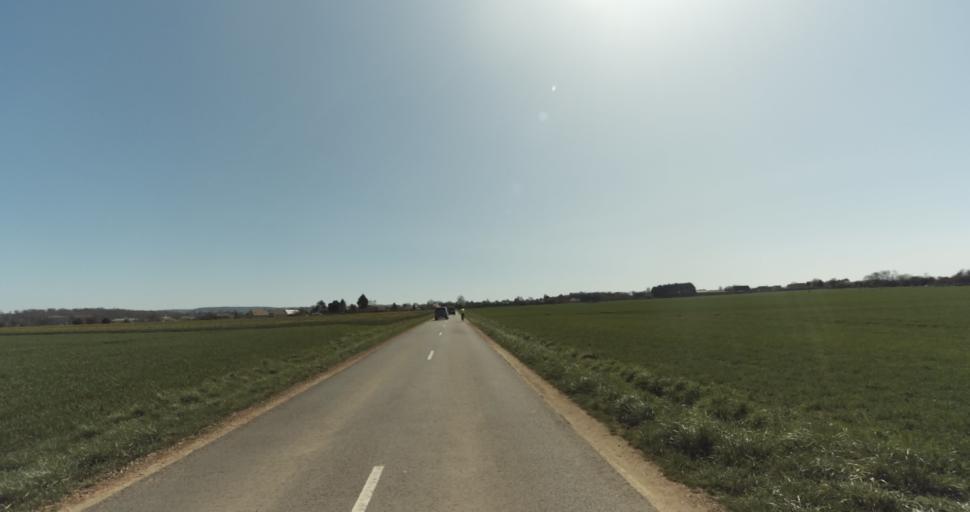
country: FR
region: Lower Normandy
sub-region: Departement du Calvados
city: Saint-Pierre-sur-Dives
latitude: 48.9957
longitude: -0.0203
